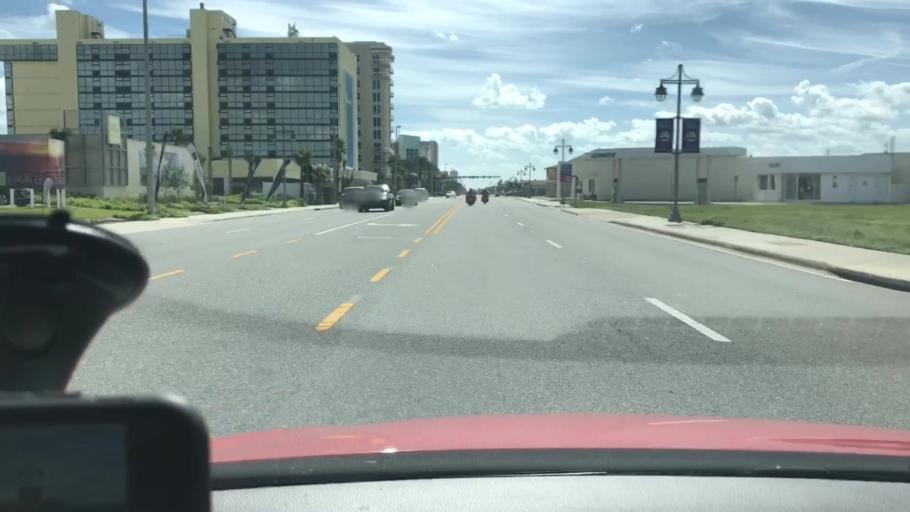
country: US
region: Florida
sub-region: Volusia County
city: Daytona Beach
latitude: 29.2062
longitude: -80.9974
